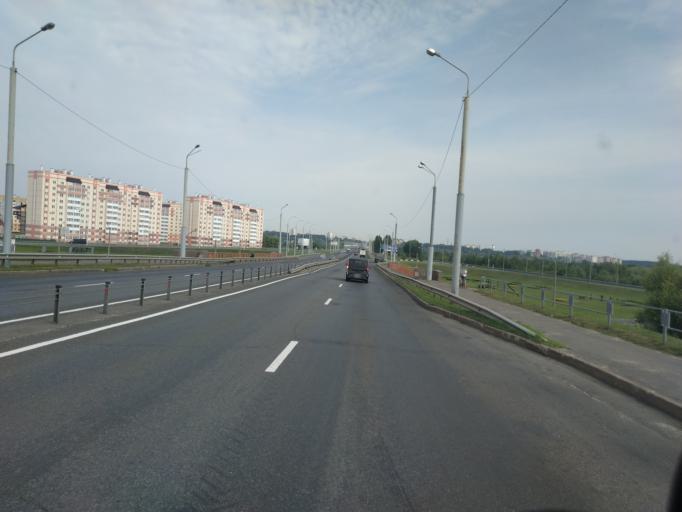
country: BY
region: Mogilev
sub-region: Mahilyowski Rayon
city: Veyno
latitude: 53.8819
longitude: 30.3816
